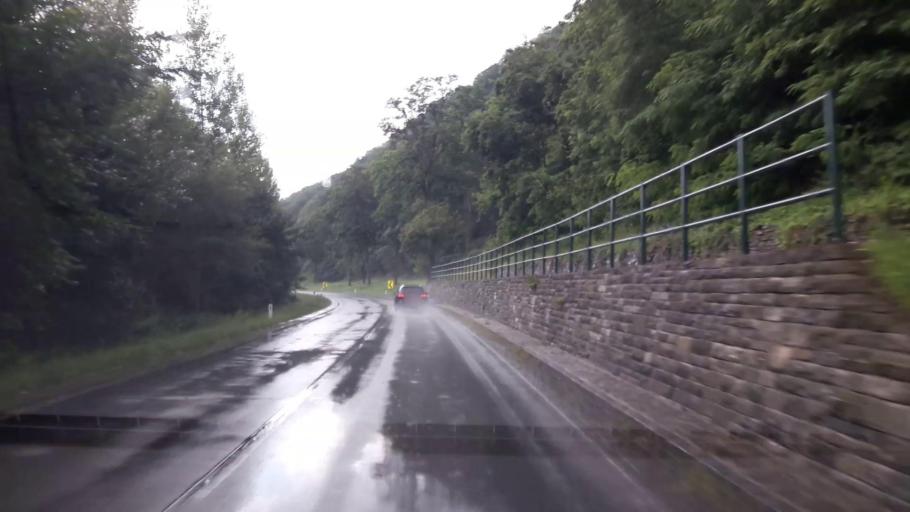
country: AT
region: Lower Austria
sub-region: Politischer Bezirk Krems
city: Aggsbach
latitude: 48.2734
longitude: 15.3788
